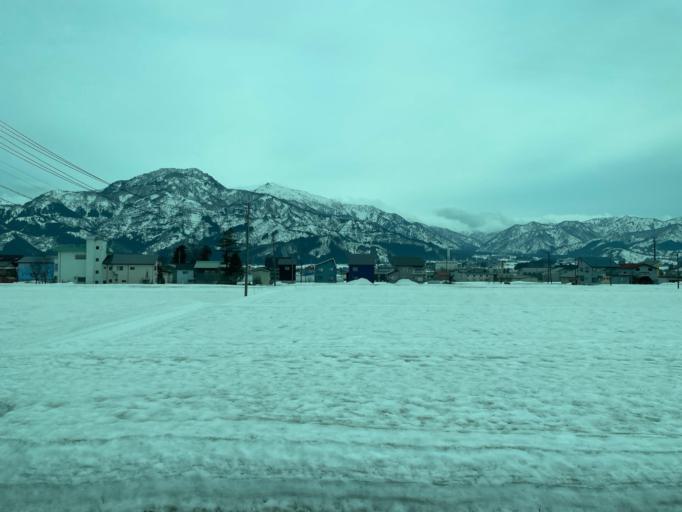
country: JP
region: Niigata
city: Shiozawa
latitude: 37.0474
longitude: 138.8590
